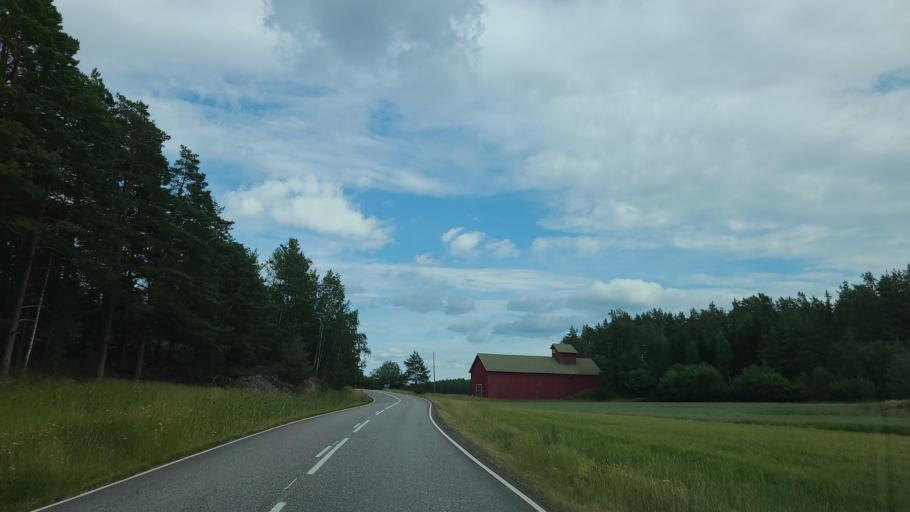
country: FI
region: Varsinais-Suomi
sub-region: Turku
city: Rymaettylae
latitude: 60.3544
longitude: 21.9552
